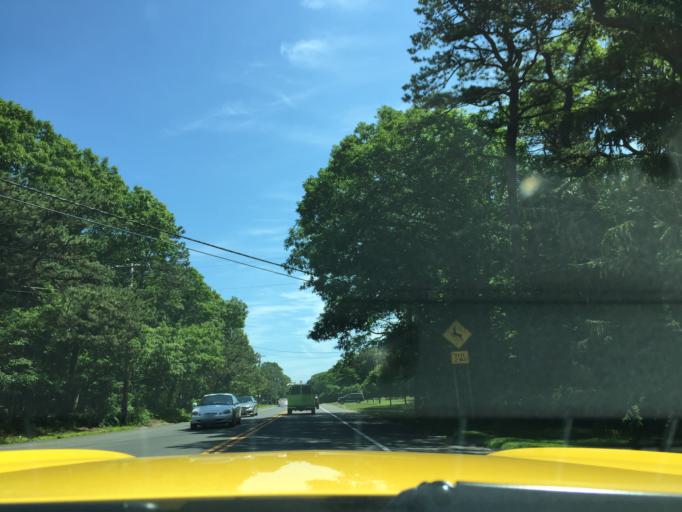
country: US
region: New York
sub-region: Suffolk County
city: East Hampton North
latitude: 40.9508
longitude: -72.2380
